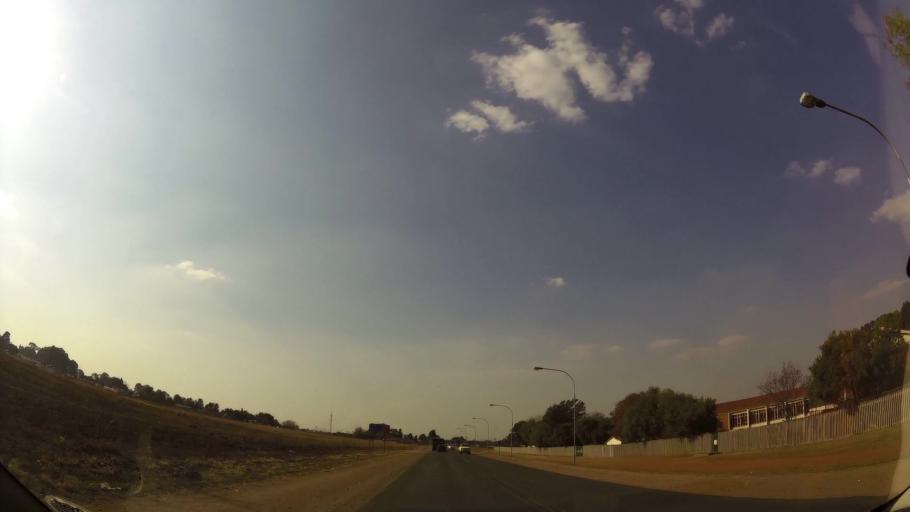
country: ZA
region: Gauteng
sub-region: Ekurhuleni Metropolitan Municipality
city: Benoni
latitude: -26.1274
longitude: 28.3908
